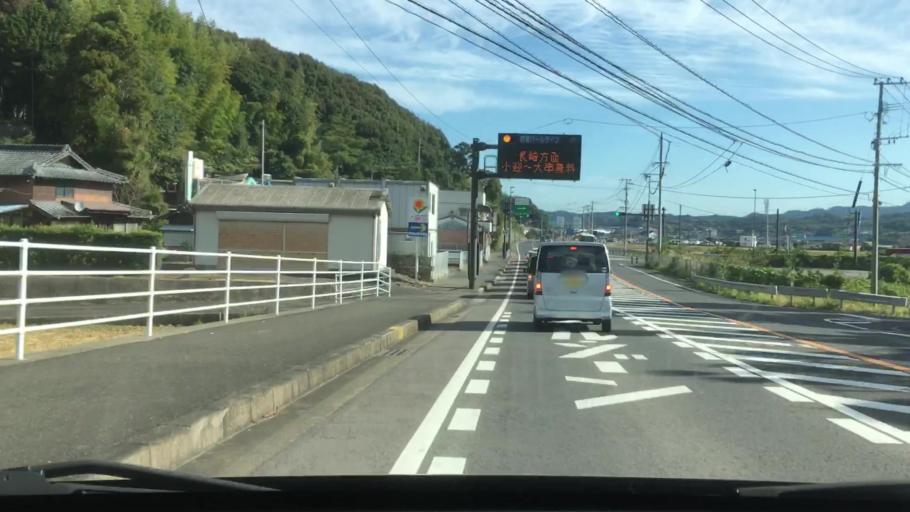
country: JP
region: Nagasaki
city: Sasebo
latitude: 33.1041
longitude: 129.7774
